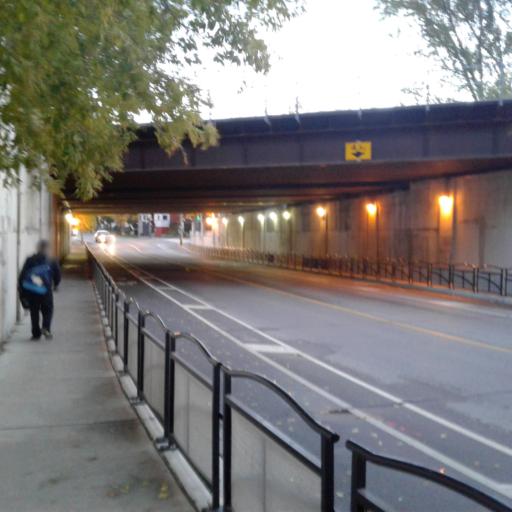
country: CA
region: Ontario
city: Toronto
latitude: 43.6479
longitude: -79.4390
